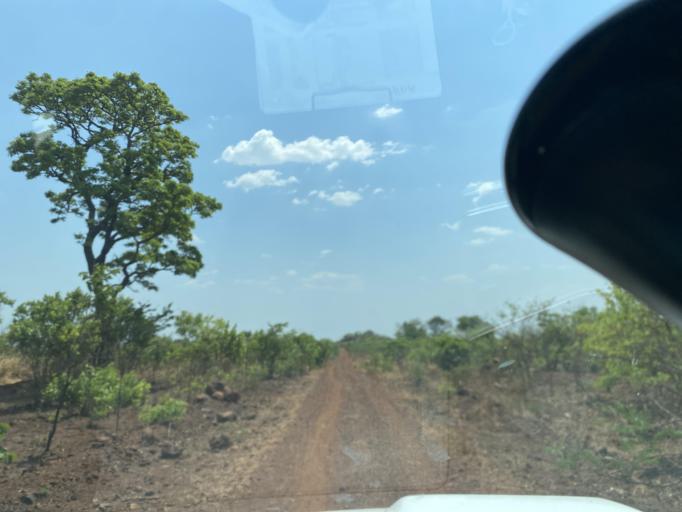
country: ZM
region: Lusaka
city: Lusaka
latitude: -15.4976
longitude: 27.9673
